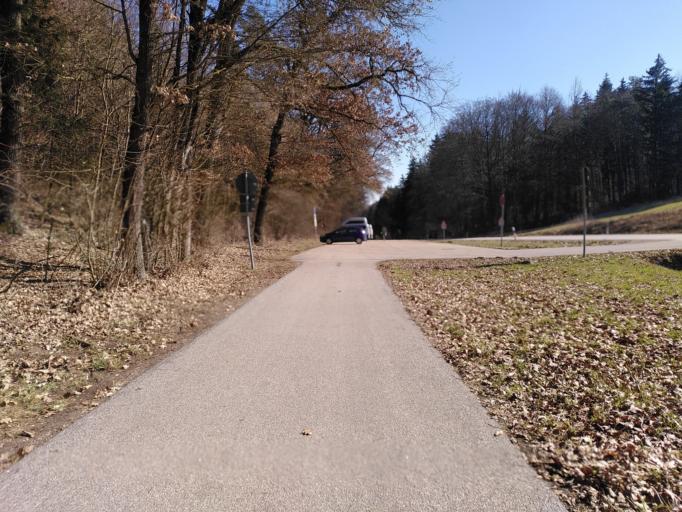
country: DE
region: Bavaria
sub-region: Upper Palatinate
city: Sinzing
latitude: 49.0018
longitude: 12.0160
